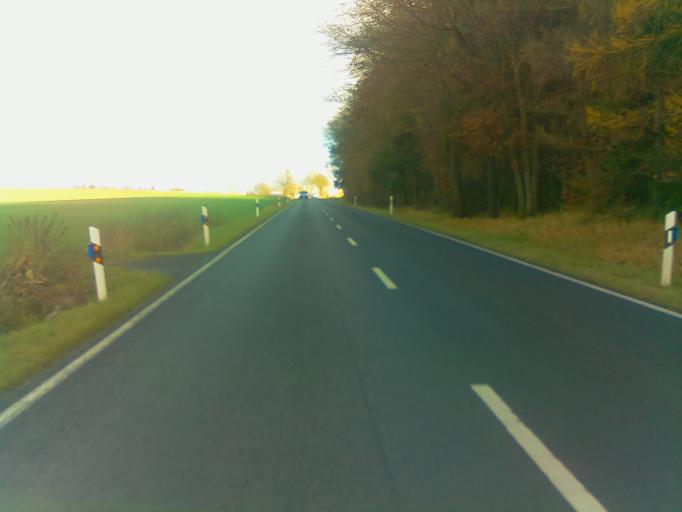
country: DE
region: Thuringia
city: Reurieth
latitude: 50.3986
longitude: 10.6681
